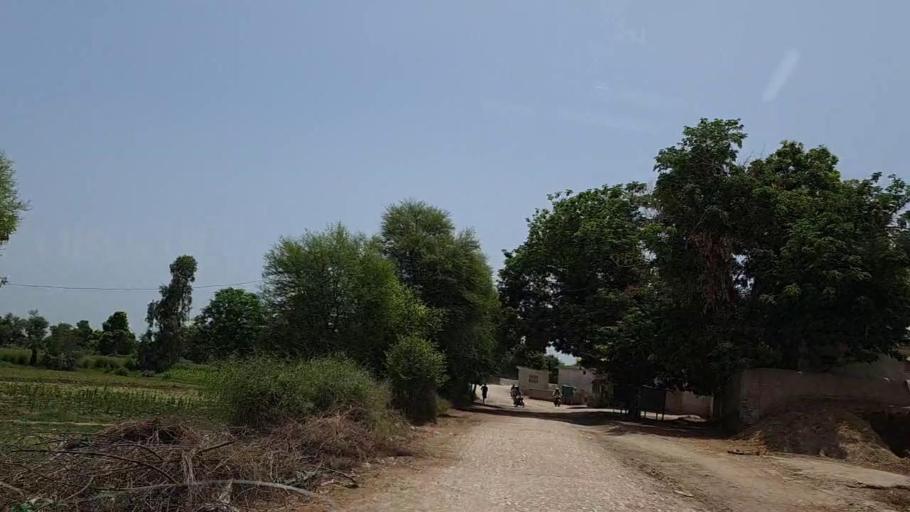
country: PK
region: Sindh
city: Tharu Shah
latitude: 26.9685
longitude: 68.0408
